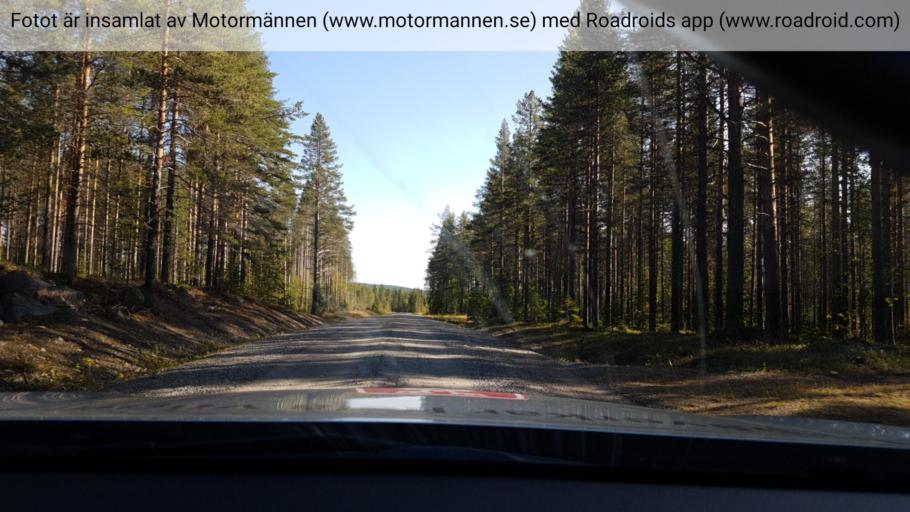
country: SE
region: Vaesterbotten
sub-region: Norsjo Kommun
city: Norsjoe
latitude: 64.6898
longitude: 19.4237
